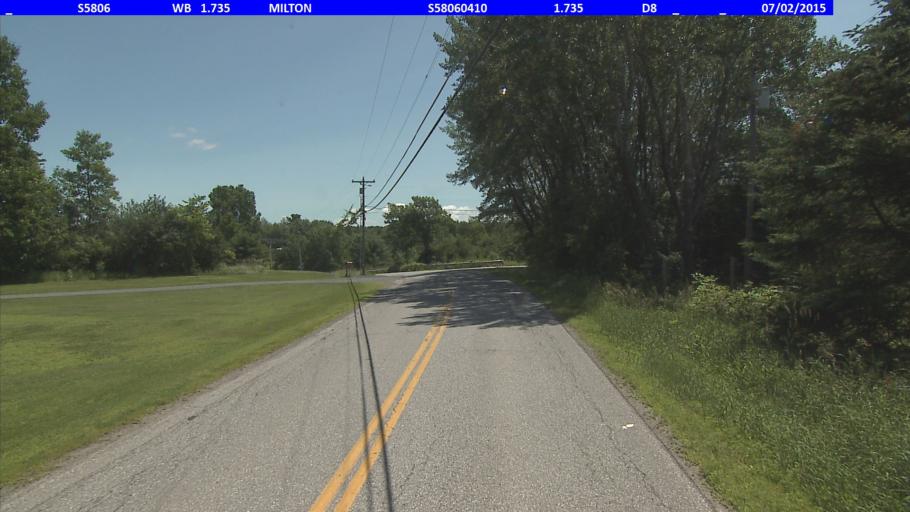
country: US
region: Vermont
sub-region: Chittenden County
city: Milton
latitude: 44.6598
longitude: -73.1450
